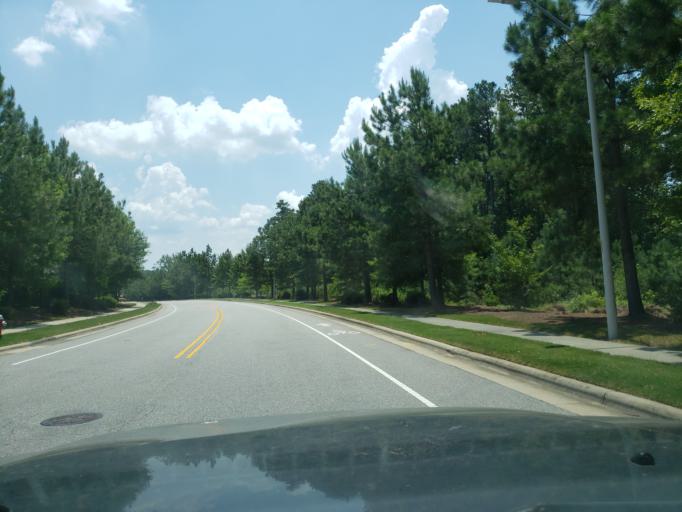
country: US
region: North Carolina
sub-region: Wake County
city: Green Level
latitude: 35.8405
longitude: -78.9146
